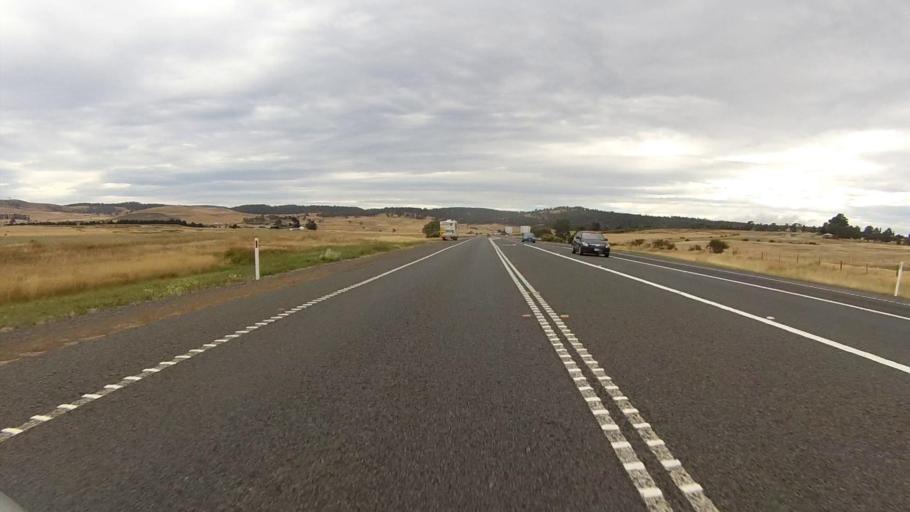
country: AU
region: Tasmania
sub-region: Brighton
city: Bridgewater
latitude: -42.3087
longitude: 147.3572
